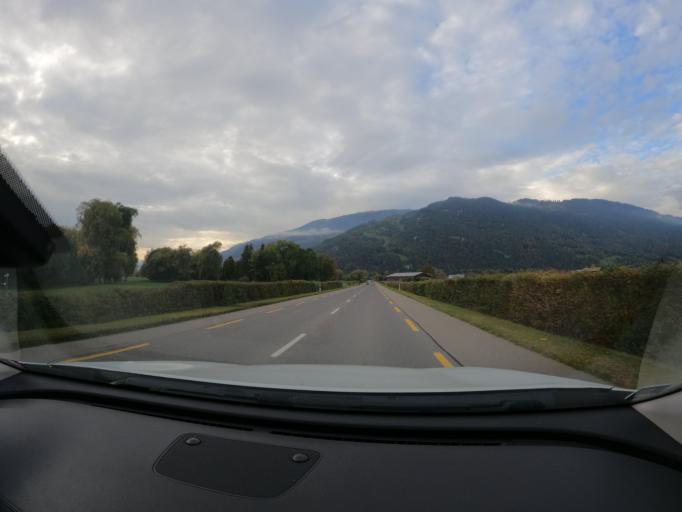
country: CH
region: Bern
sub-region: Interlaken-Oberhasli District
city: Unterseen
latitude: 46.6749
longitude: 7.8329
